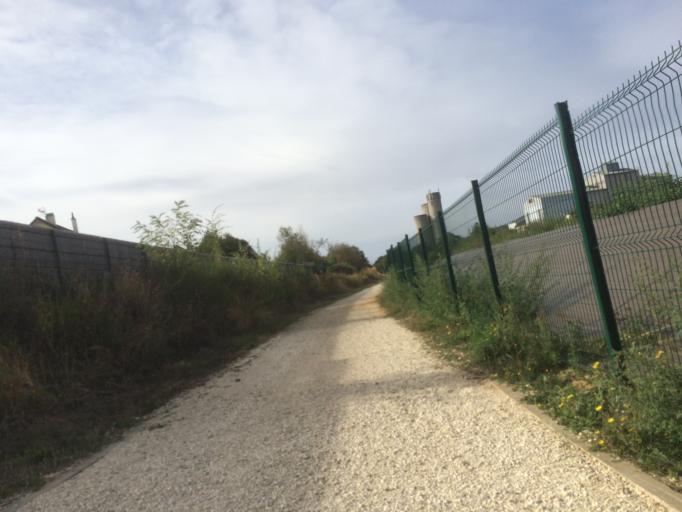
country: FR
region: Ile-de-France
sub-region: Departement de l'Essonne
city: Limours
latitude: 48.6441
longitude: 2.0637
